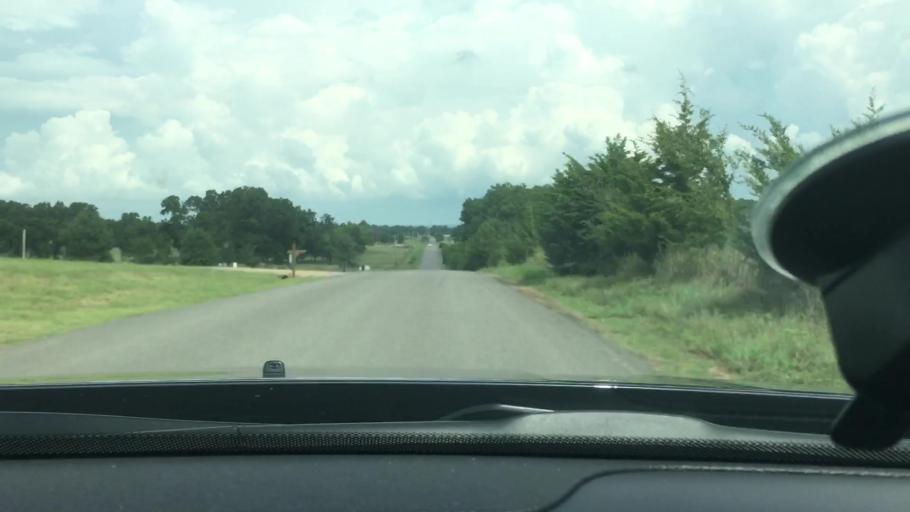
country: US
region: Oklahoma
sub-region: Carter County
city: Dickson
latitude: 34.1894
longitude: -96.8982
